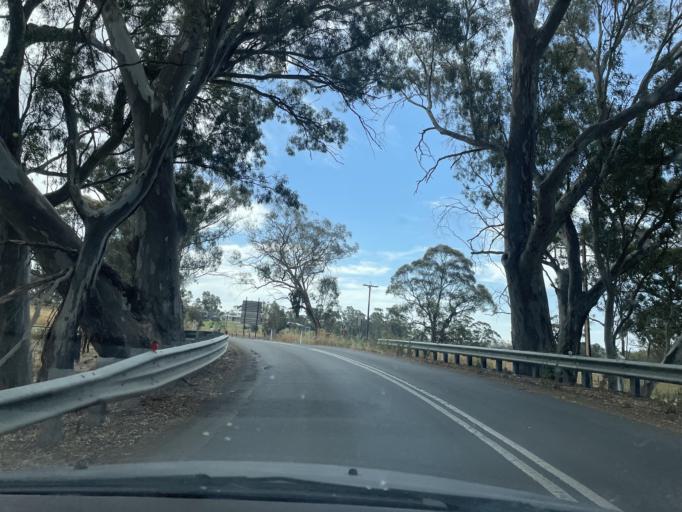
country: AU
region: South Australia
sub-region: Clare and Gilbert Valleys
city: Clare
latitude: -33.8963
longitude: 138.6371
